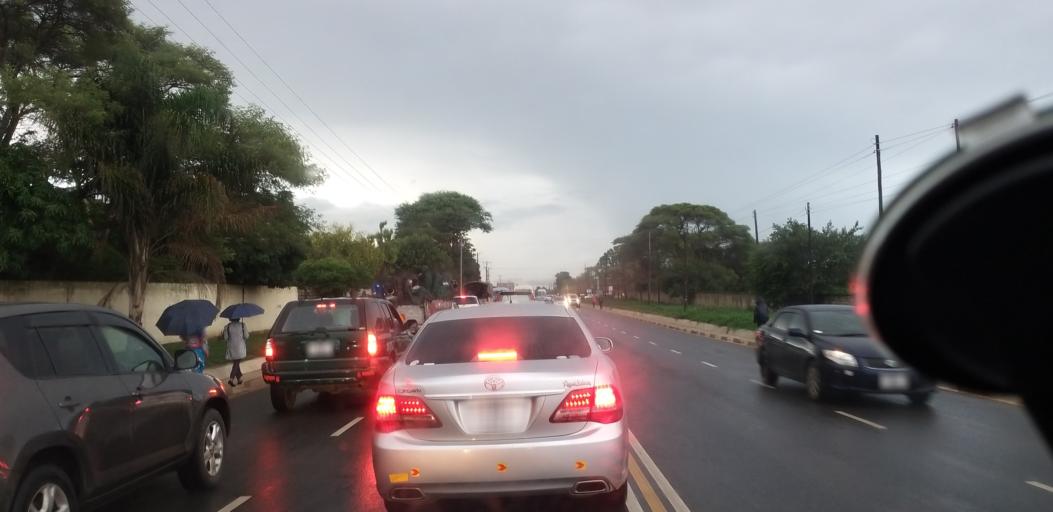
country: ZM
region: Lusaka
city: Lusaka
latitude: -15.4296
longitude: 28.3556
